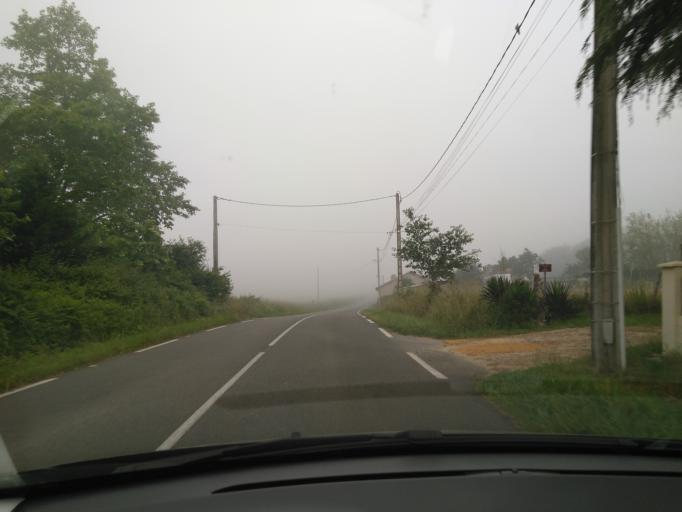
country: FR
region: Aquitaine
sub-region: Departement des Landes
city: Villeneuve-de-Marsan
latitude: 43.8864
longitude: -0.3309
